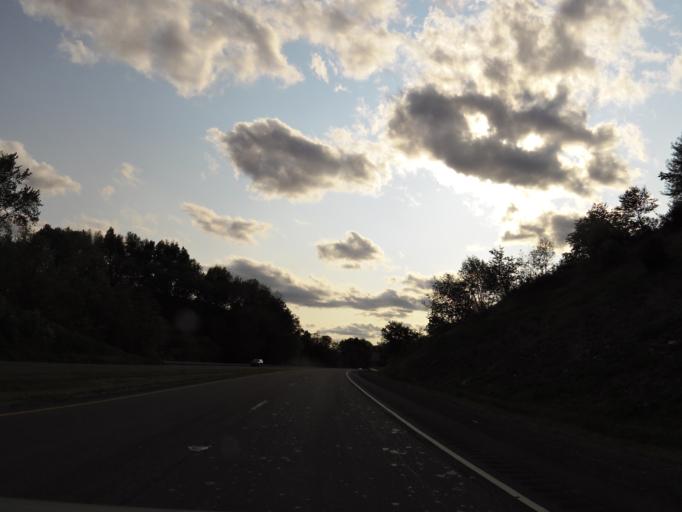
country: US
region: Virginia
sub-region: Tazewell County
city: Tazewell
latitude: 37.1198
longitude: -81.5516
